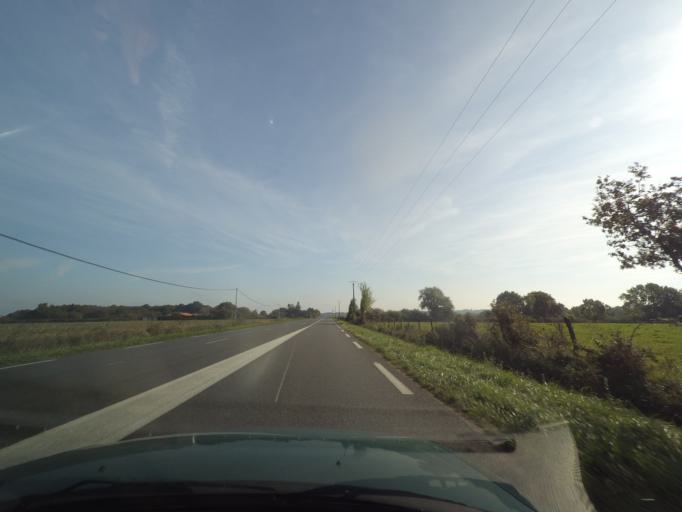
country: FR
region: Pays de la Loire
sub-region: Departement de Maine-et-Loire
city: Vihiers
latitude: 47.1510
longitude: -0.4620
